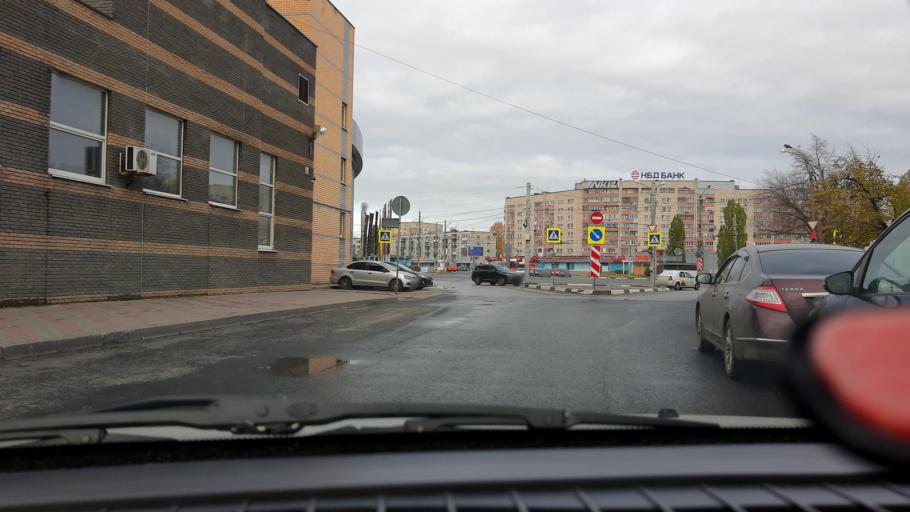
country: RU
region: Nizjnij Novgorod
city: Nizhniy Novgorod
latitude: 56.3186
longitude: 43.9288
